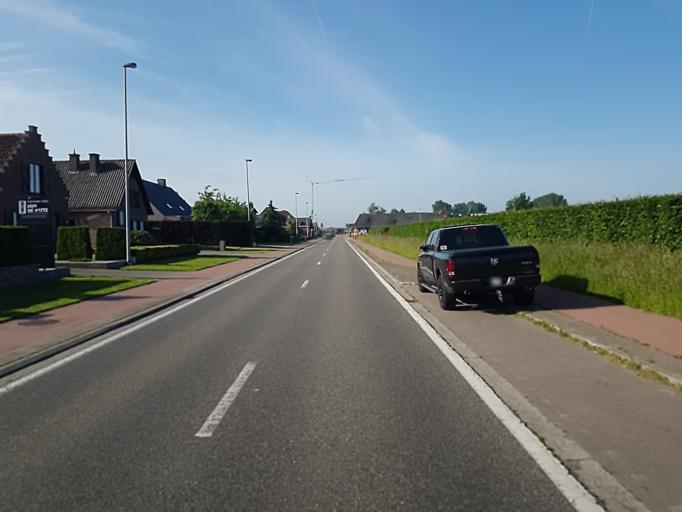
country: BE
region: Flanders
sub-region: Provincie Oost-Vlaanderen
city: Beveren
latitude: 51.2084
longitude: 4.1930
